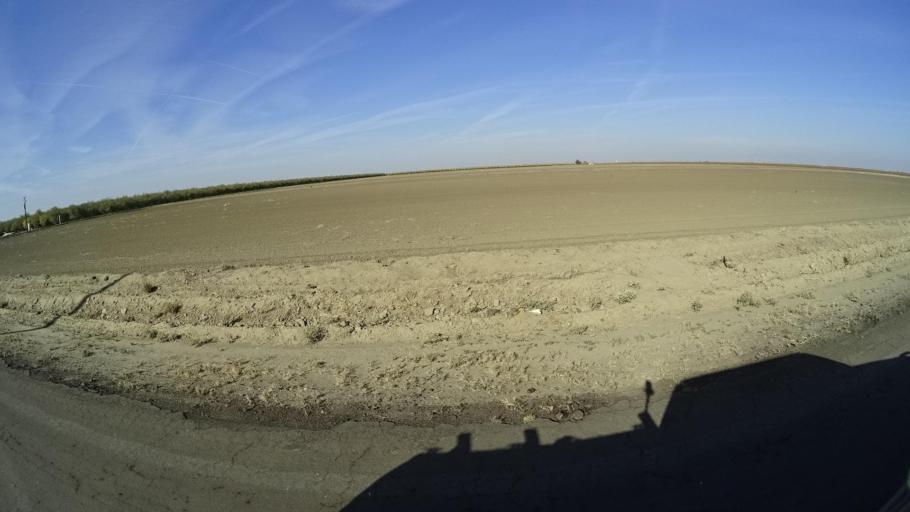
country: US
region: California
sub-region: Kern County
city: Wasco
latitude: 35.6886
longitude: -119.3959
